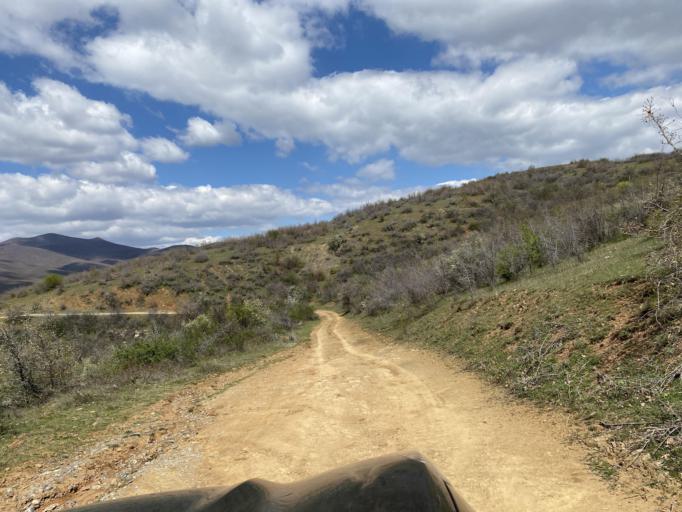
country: MK
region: Caska
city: Caska
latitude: 41.7291
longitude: 21.6607
